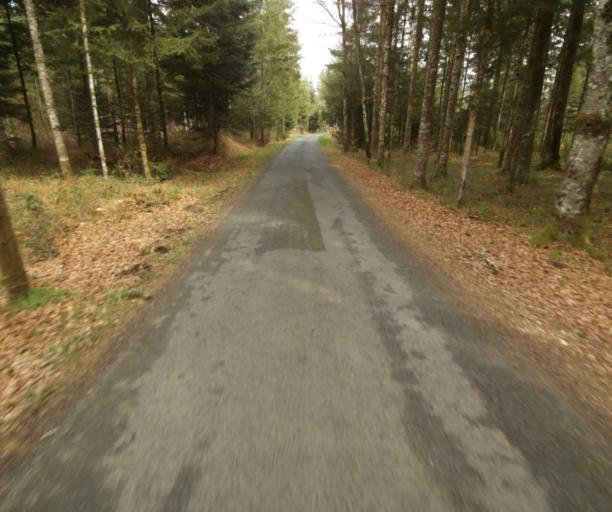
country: FR
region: Limousin
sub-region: Departement de la Correze
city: Correze
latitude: 45.3258
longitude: 1.8990
